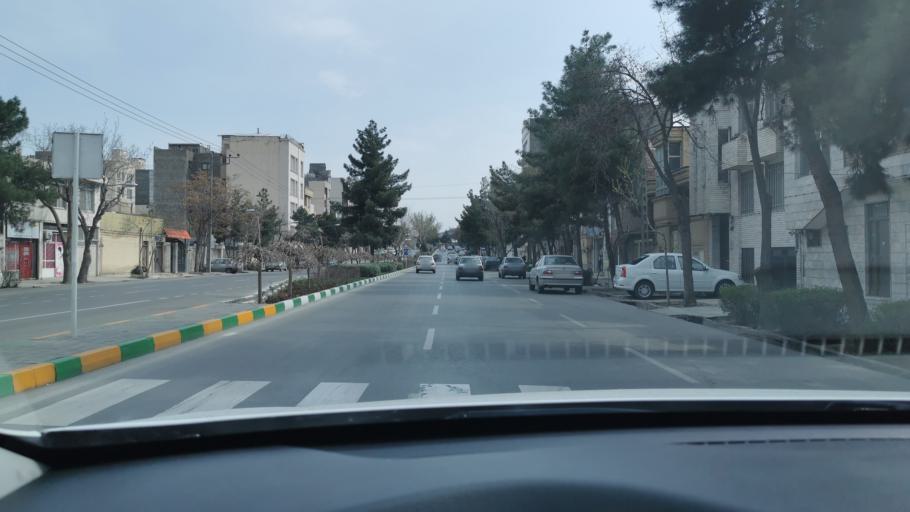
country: IR
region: Razavi Khorasan
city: Mashhad
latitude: 36.2776
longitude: 59.5657
